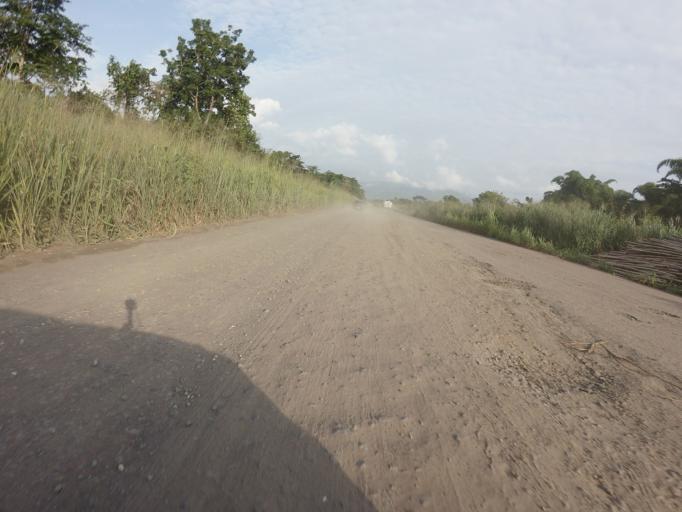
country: GH
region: Volta
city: Kpandu
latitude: 6.9749
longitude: 0.4506
